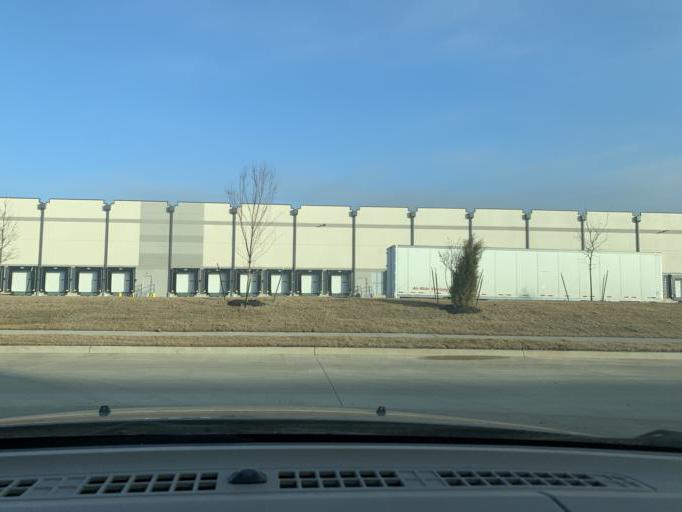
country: US
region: Texas
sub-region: Dallas County
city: Carrollton
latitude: 32.9542
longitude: -96.9227
